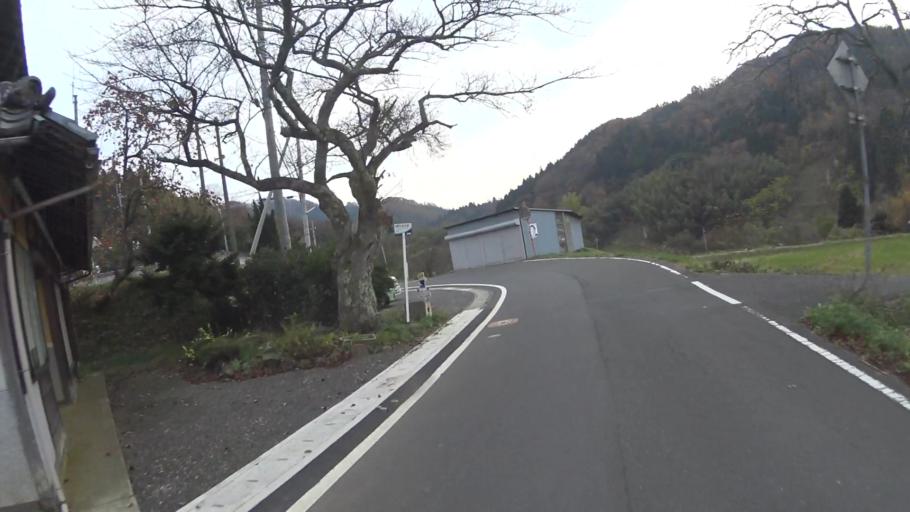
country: JP
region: Kyoto
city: Maizuru
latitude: 35.5501
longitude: 135.4498
